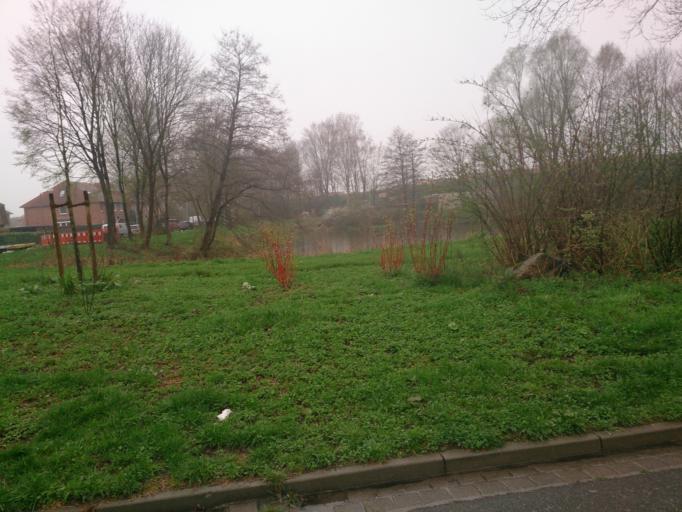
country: DE
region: Lower Saxony
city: Neu Wulmstorf
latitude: 53.4725
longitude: 9.7980
